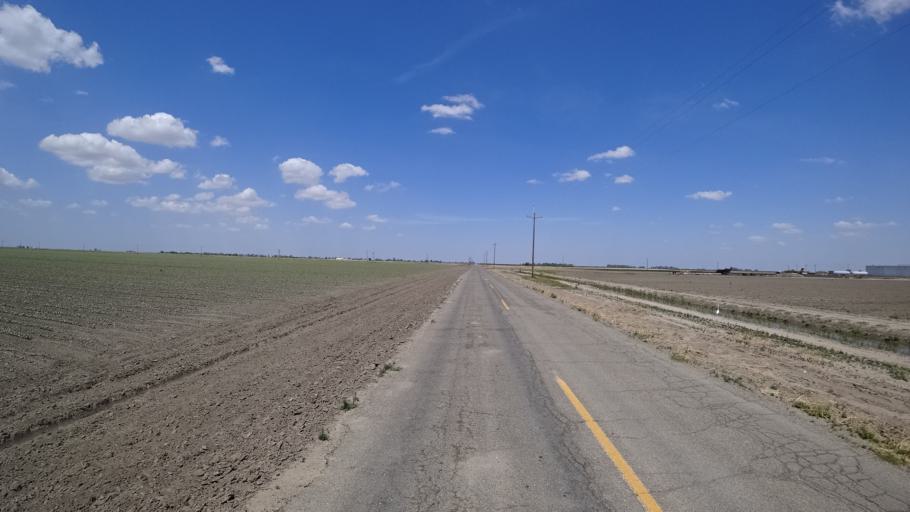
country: US
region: California
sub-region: Kings County
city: Stratford
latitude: 36.1642
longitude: -119.8161
